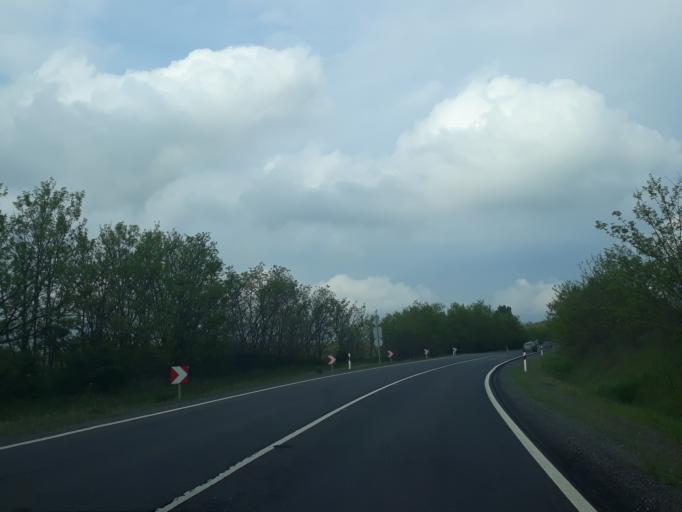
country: HU
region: Szabolcs-Szatmar-Bereg
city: Nyirtass
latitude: 48.1415
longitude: 22.0235
